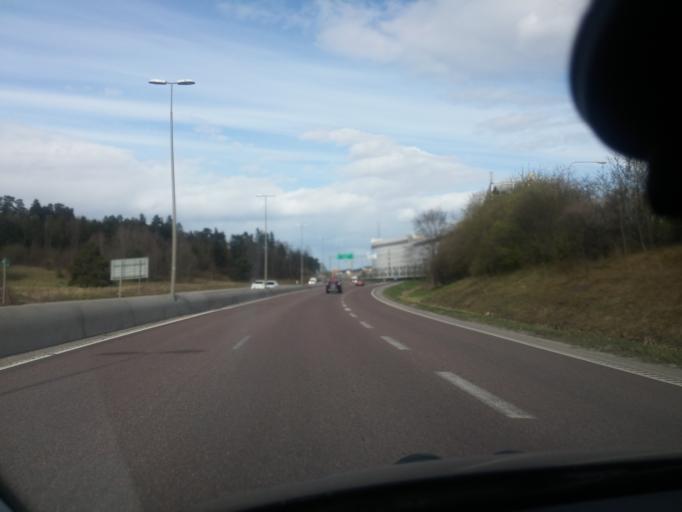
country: SE
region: Stockholm
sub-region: Stockholms Kommun
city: Kista
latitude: 59.3785
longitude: 17.9292
